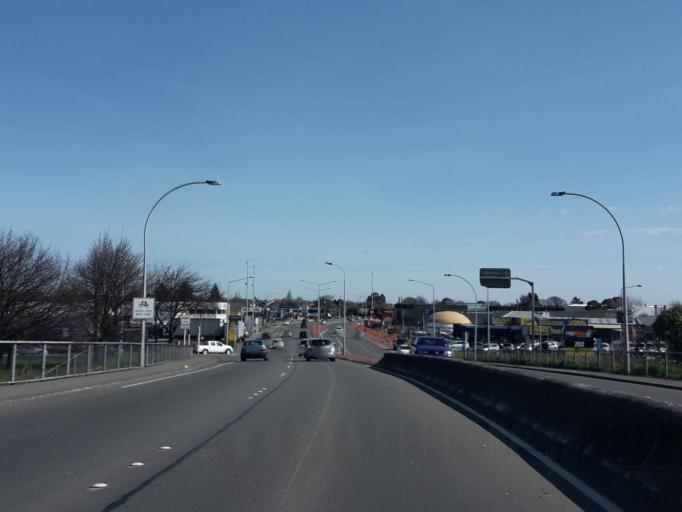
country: NZ
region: Canterbury
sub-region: Selwyn District
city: Prebbleton
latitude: -43.5412
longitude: 172.5497
